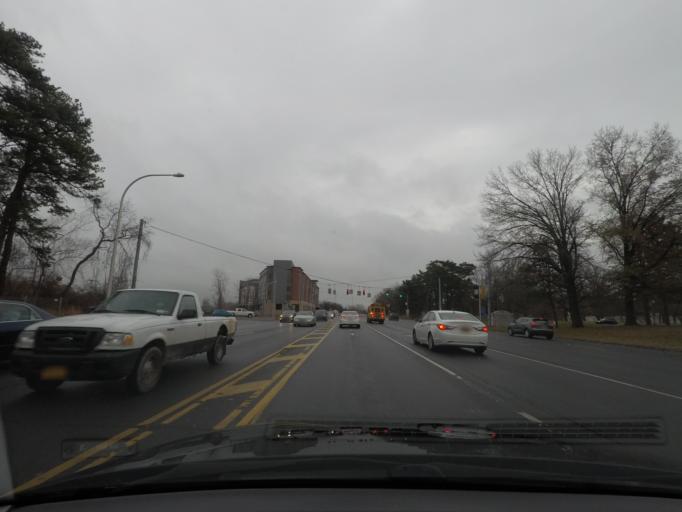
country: US
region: New York
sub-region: Albany County
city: Roessleville
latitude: 42.6916
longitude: -73.8248
